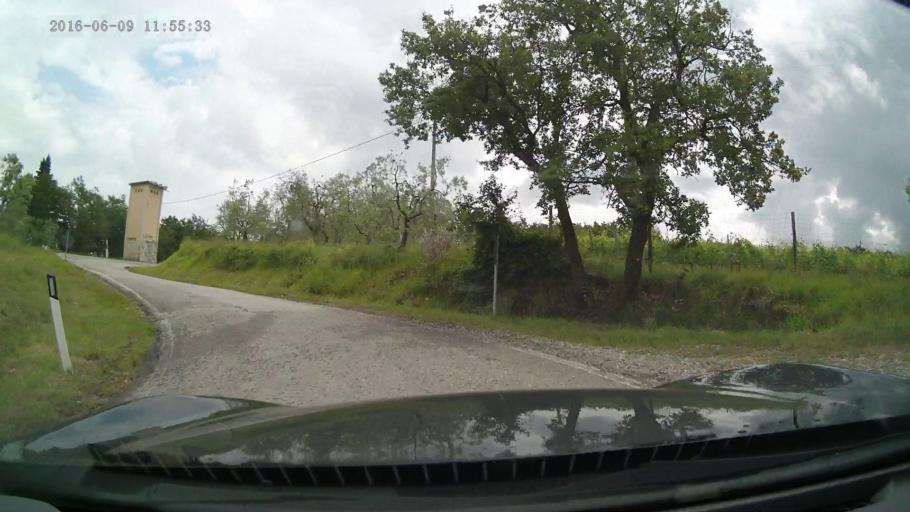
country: IT
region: Tuscany
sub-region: Province of Florence
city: Panzano in Chianti
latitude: 43.5643
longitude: 11.2911
